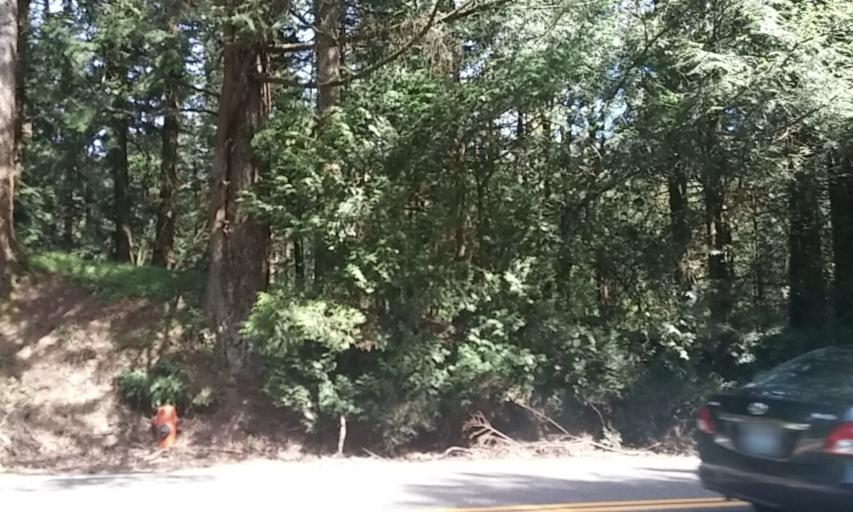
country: US
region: Oregon
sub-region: Washington County
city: West Haven-Sylvan
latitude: 45.5154
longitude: -122.7290
